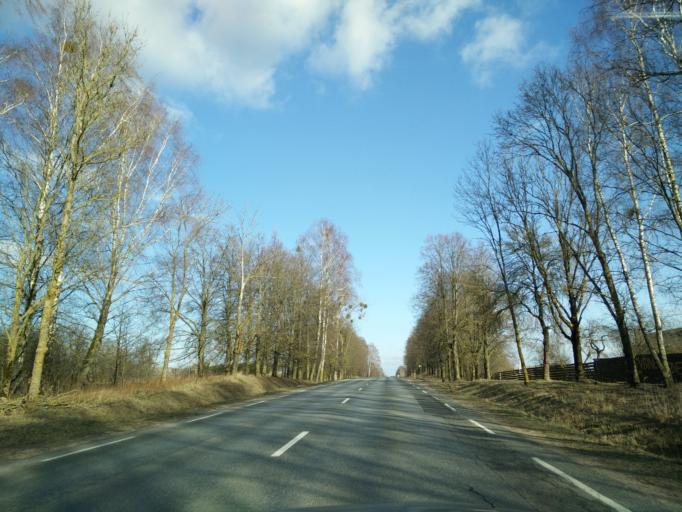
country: LT
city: Kulautuva
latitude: 54.9513
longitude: 23.7003
